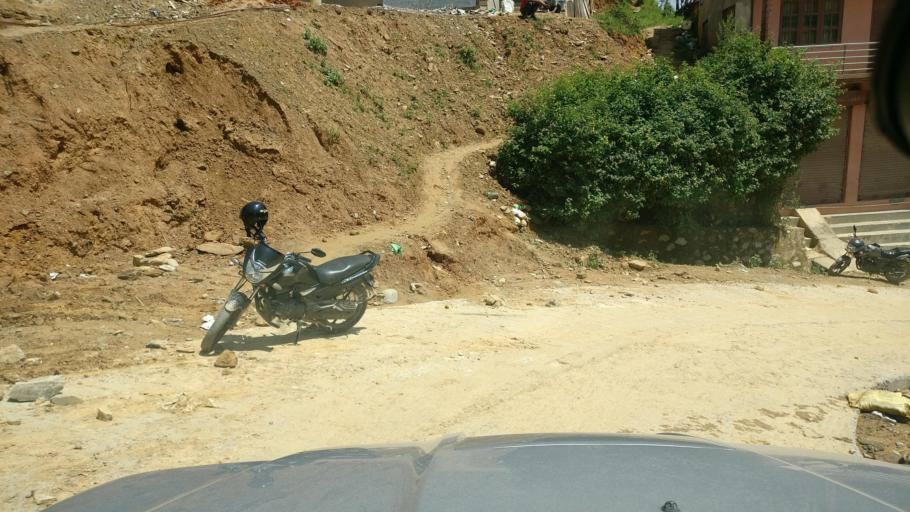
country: NP
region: Central Region
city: Kirtipur
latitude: 27.7029
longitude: 85.2576
